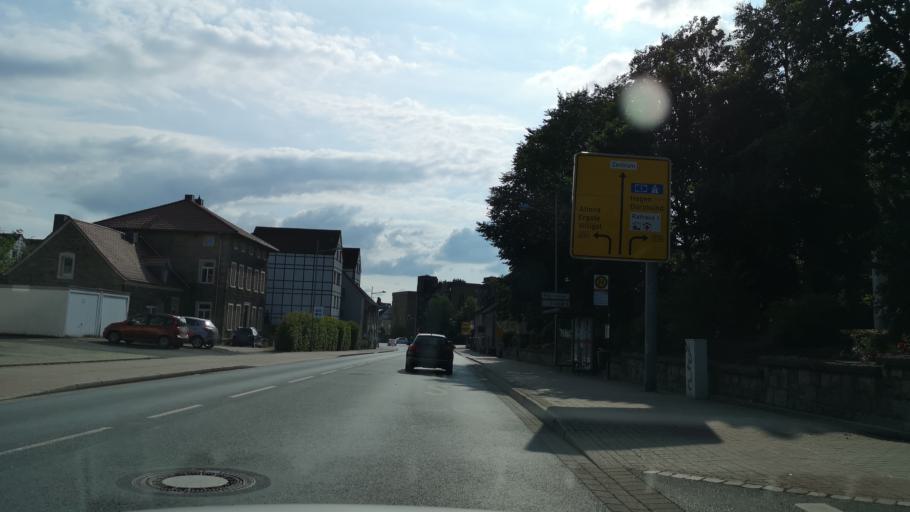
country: DE
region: North Rhine-Westphalia
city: Schwerte
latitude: 51.4441
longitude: 7.5756
